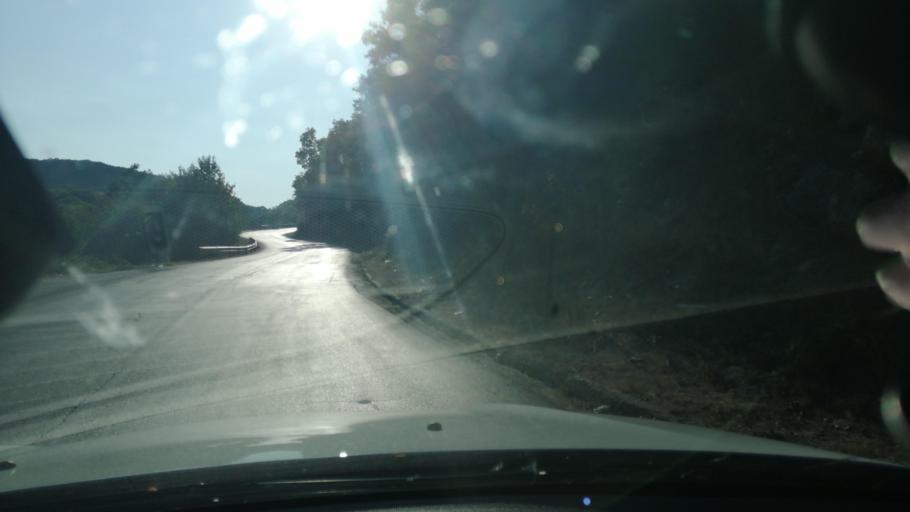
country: RS
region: Central Serbia
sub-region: Moravicki Okrug
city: Ivanjica
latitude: 43.6354
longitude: 20.2453
